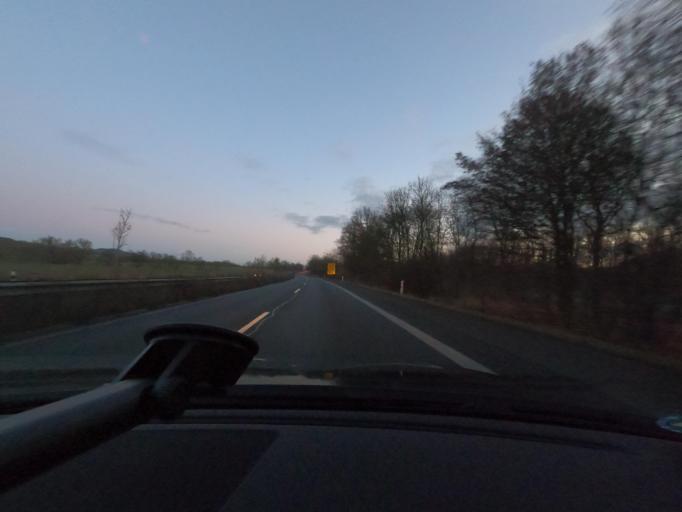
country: DE
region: Lower Saxony
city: Herzberg am Harz
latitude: 51.6696
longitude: 10.3162
